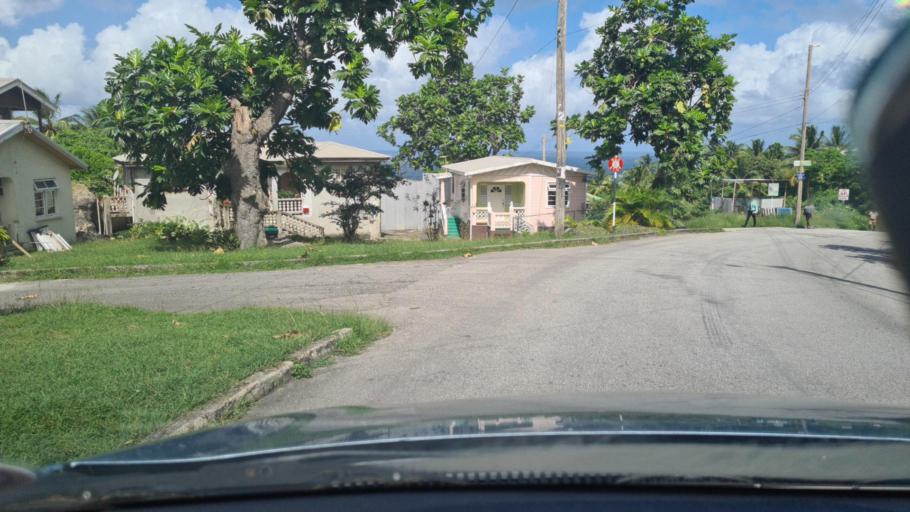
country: BB
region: Saint Joseph
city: Bathsheba
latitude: 13.2081
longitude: -59.5309
